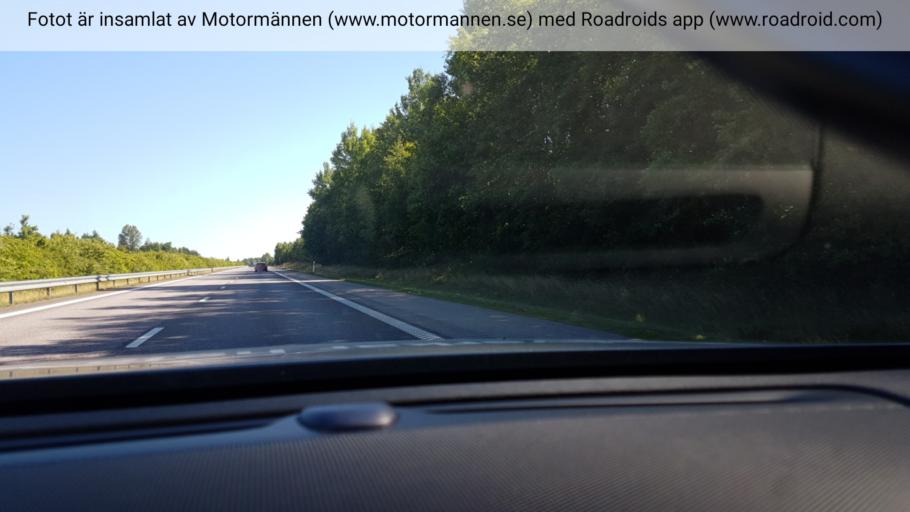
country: SE
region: Kronoberg
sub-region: Markaryds Kommun
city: Stromsnasbruk
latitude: 56.6703
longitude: 13.8225
